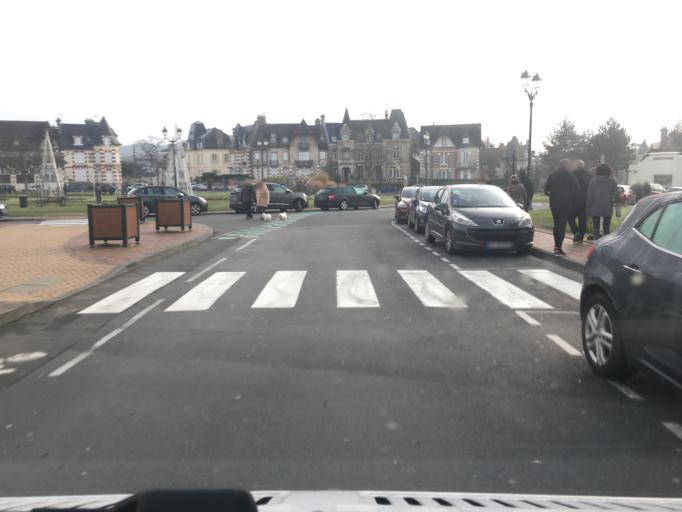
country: FR
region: Lower Normandy
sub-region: Departement du Calvados
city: Cabourg
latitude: 49.2933
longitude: -0.1164
